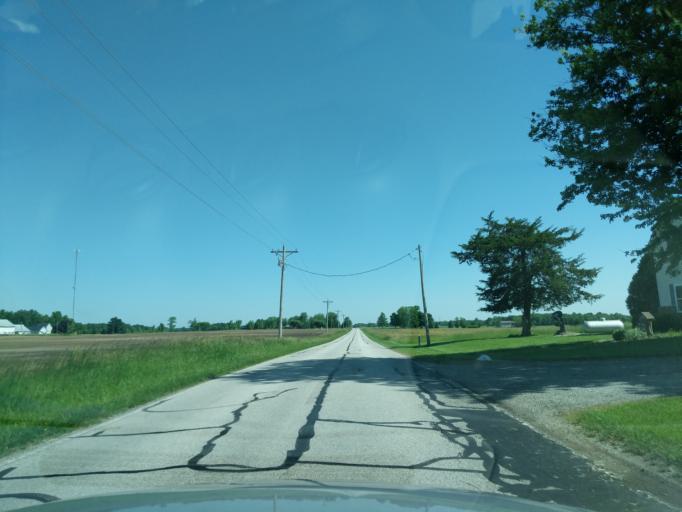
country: US
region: Indiana
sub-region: Huntington County
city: Warren
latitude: 40.6923
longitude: -85.5069
